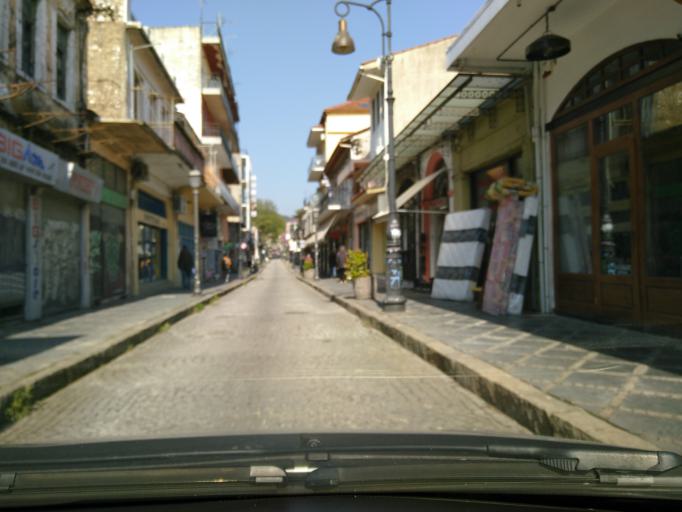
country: GR
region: Epirus
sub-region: Nomos Ioanninon
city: Ioannina
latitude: 39.6698
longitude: 20.8532
